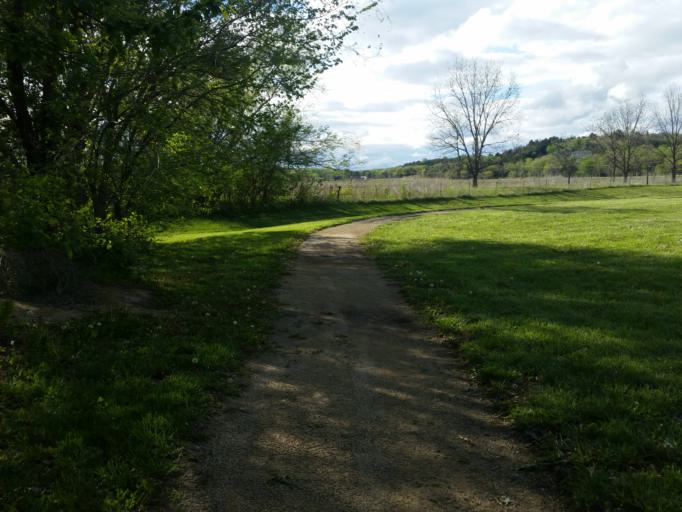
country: US
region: Kansas
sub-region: Riley County
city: Ogden
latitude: 39.2232
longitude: -96.7119
